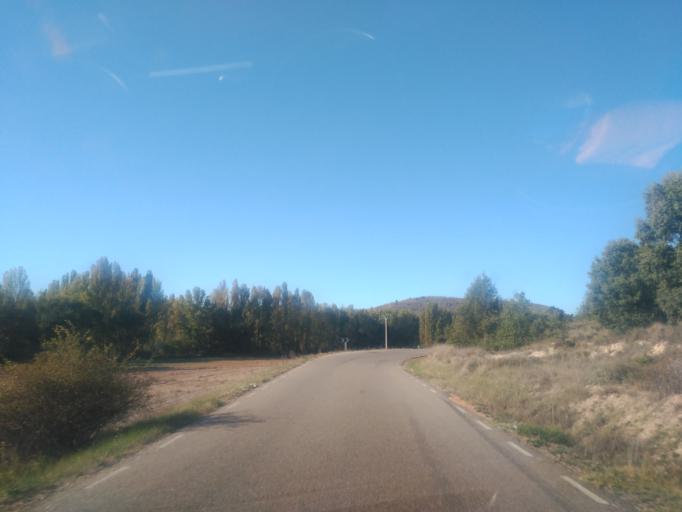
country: ES
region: Castille and Leon
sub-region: Provincia de Burgos
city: Penaranda de Duero
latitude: 41.6846
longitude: -3.4286
